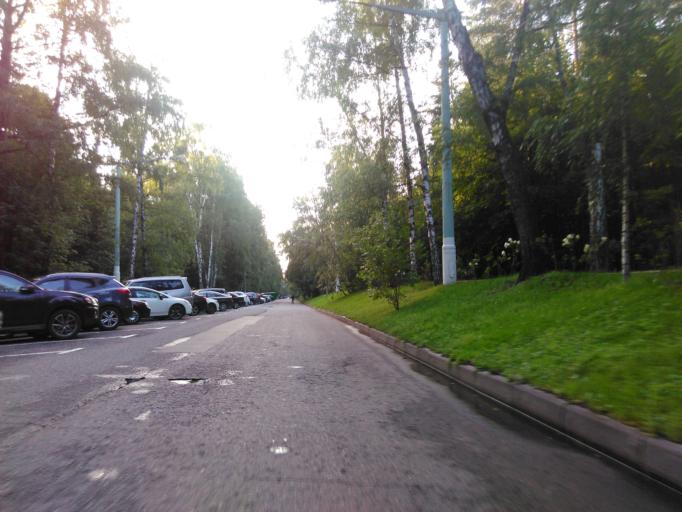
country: RU
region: Moscow
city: Sokol'niki
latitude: 55.7996
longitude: 37.6700
